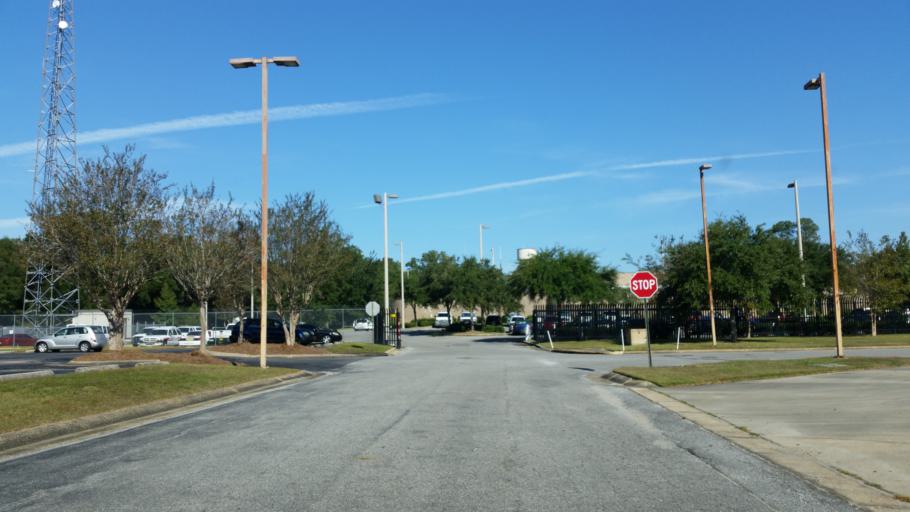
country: US
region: Florida
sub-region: Escambia County
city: Brent
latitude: 30.4824
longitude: -87.2612
